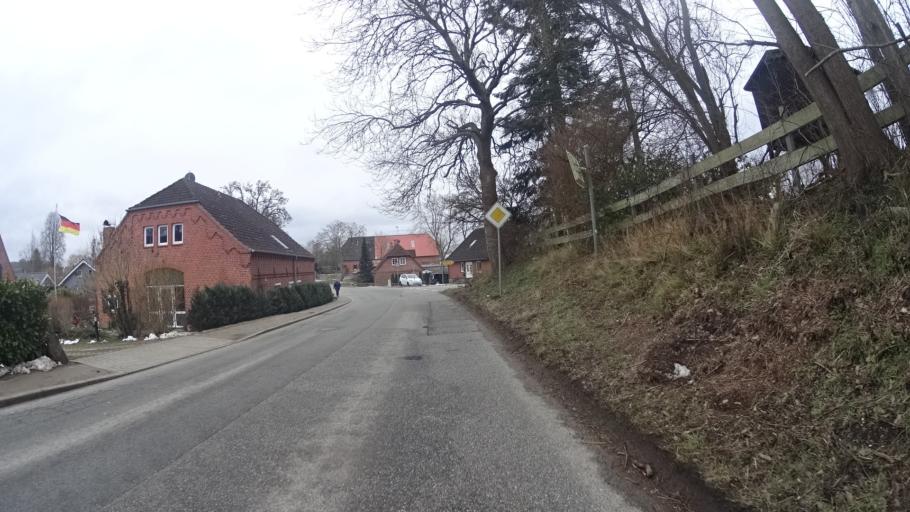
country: DE
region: Schleswig-Holstein
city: Neukirchen
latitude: 54.2053
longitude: 10.5574
